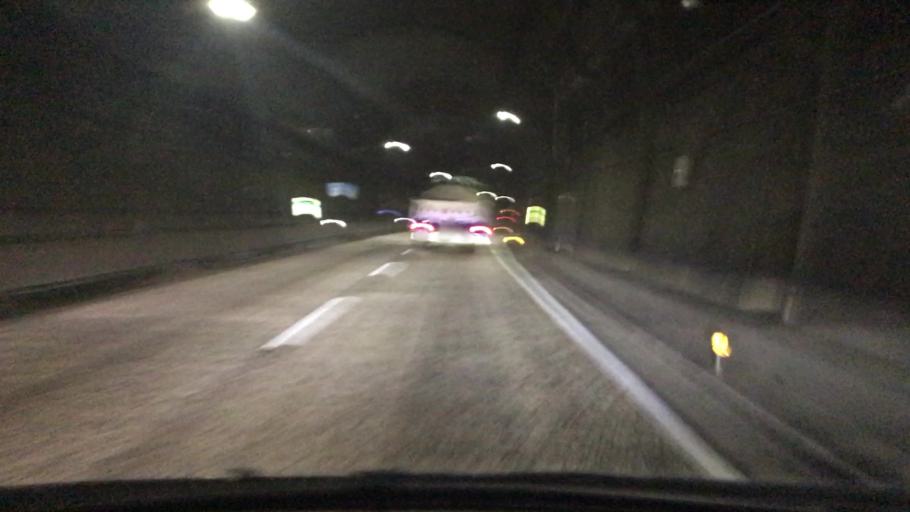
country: JP
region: Hyogo
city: Kobe
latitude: 34.7502
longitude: 135.1674
